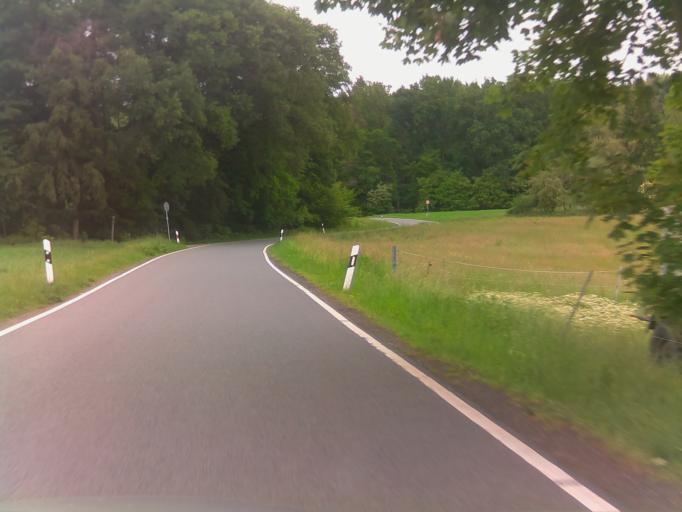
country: DE
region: Bavaria
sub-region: Regierungsbezirk Unterfranken
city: Johannesberg
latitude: 50.0062
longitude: 9.1182
